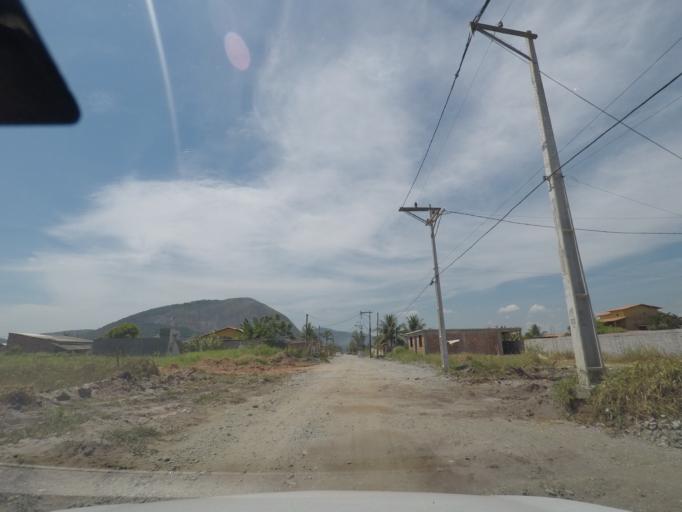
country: BR
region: Rio de Janeiro
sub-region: Marica
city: Marica
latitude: -22.9588
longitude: -42.9550
